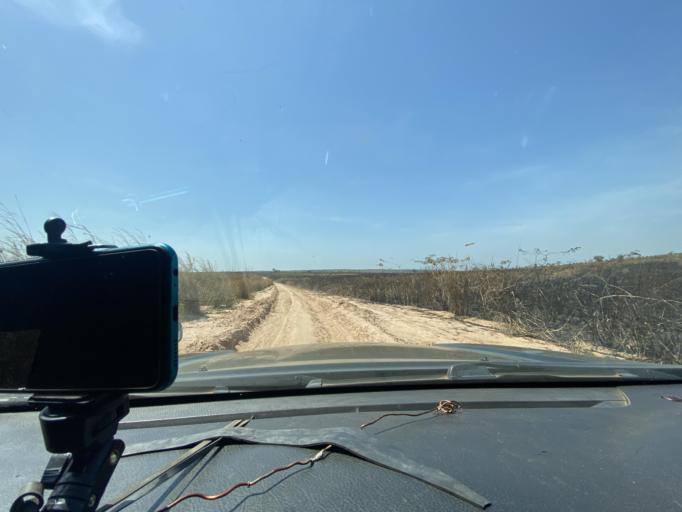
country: CD
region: Kasai-Oriental
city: Kabinda
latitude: -5.9397
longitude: 24.8123
